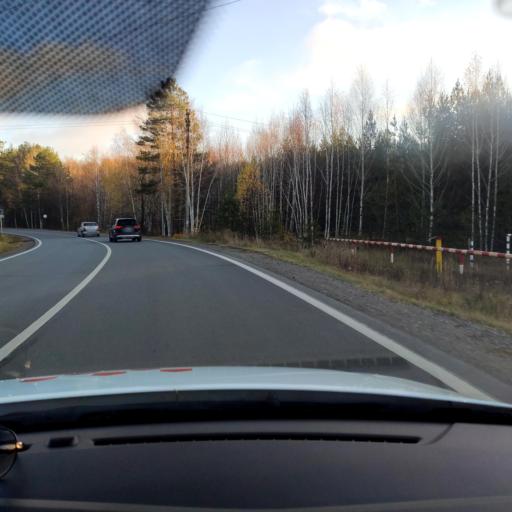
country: RU
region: Tatarstan
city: Verkhniy Uslon
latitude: 55.6363
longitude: 49.0217
